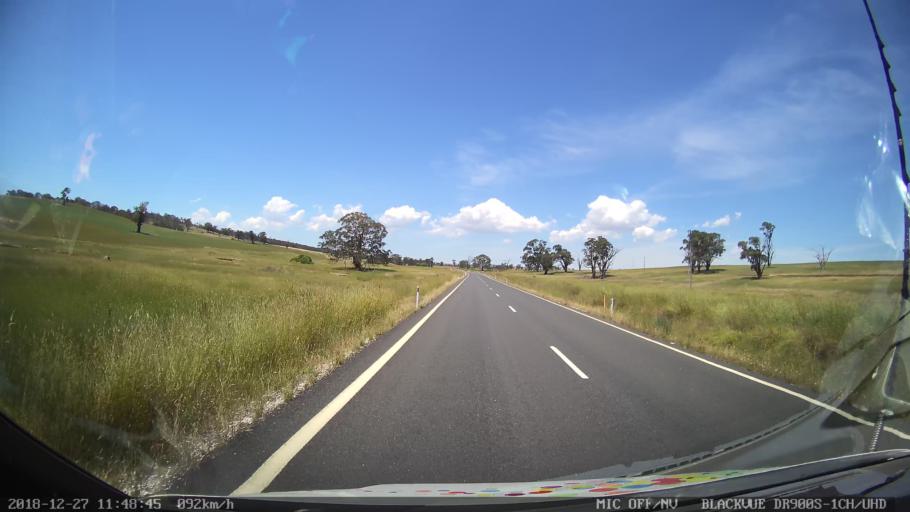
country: AU
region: New South Wales
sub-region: Bathurst Regional
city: Perthville
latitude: -33.6106
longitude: 149.4356
